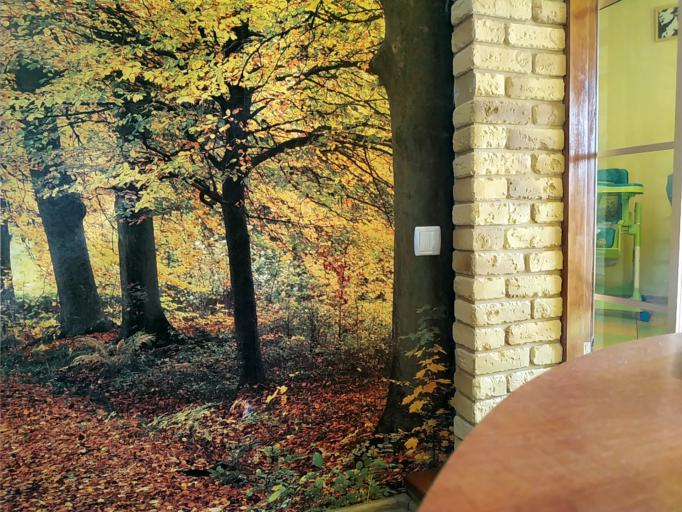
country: RU
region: Novgorod
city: Parfino
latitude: 57.8070
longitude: 31.5863
